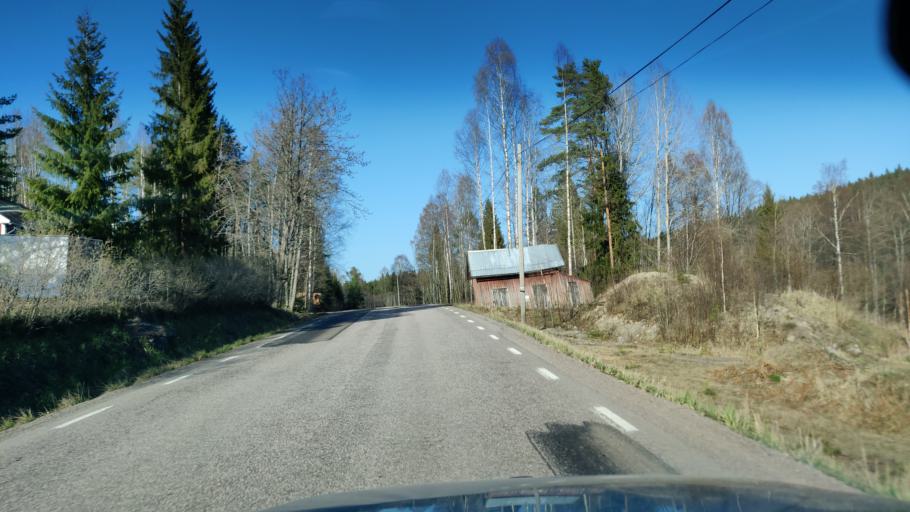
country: SE
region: Vaermland
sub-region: Sunne Kommun
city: Sunne
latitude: 59.9841
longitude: 13.2634
